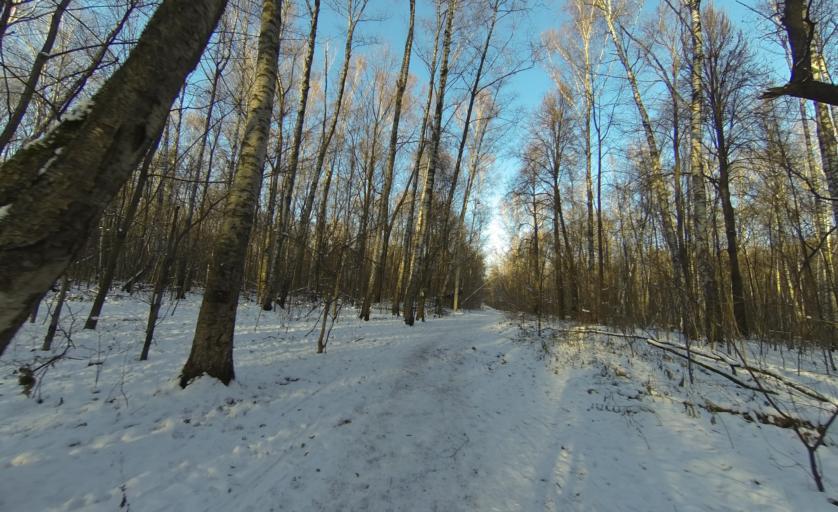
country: RU
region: Moscow
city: Rostokino
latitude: 55.8211
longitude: 37.6848
